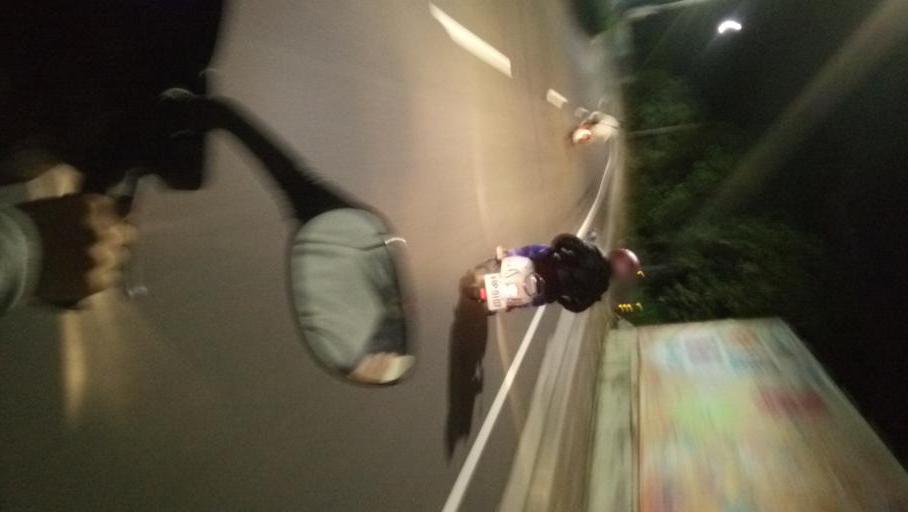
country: TW
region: Taiwan
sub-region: Hsinchu
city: Zhubei
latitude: 24.7175
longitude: 121.1457
